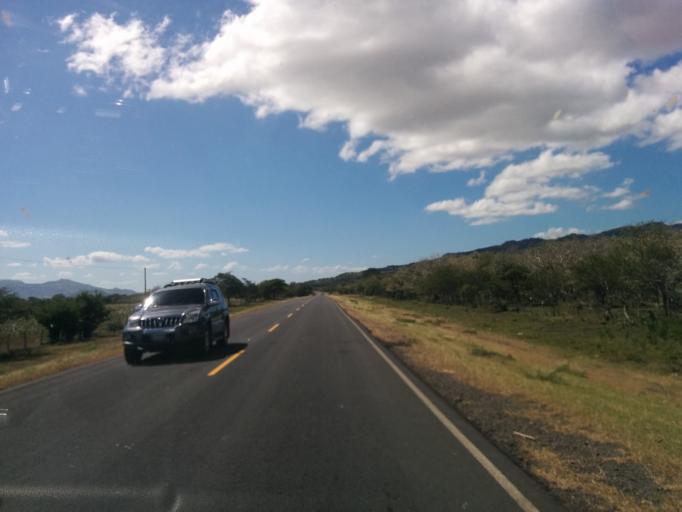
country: NI
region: Matagalpa
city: Ciudad Dario
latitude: 12.8569
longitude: -86.2049
